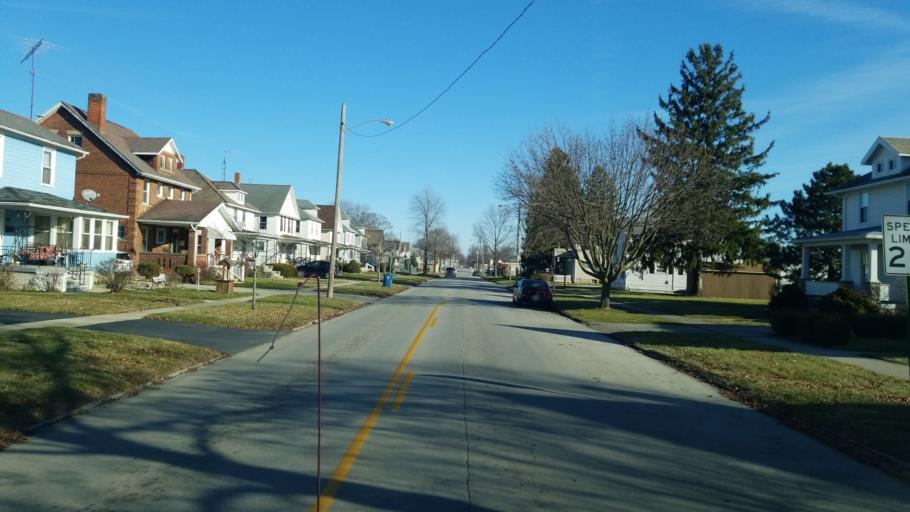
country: US
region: Ohio
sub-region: Sandusky County
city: Fremont
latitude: 41.3485
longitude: -83.1318
